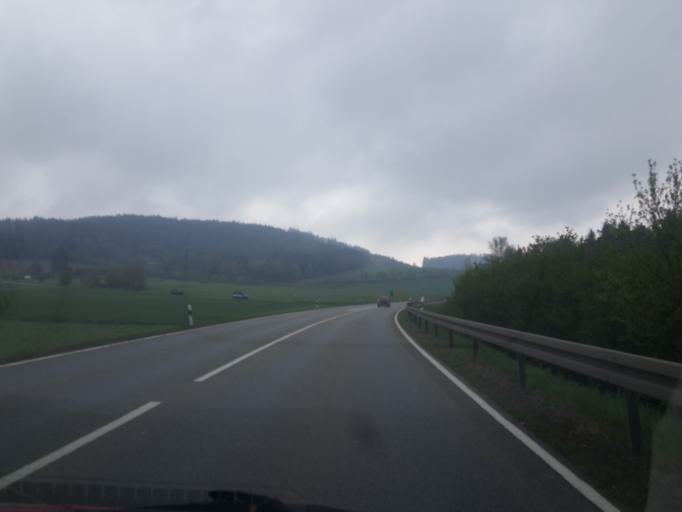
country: DE
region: Bavaria
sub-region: Lower Bavaria
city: Geiersthal
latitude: 49.0449
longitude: 12.9340
